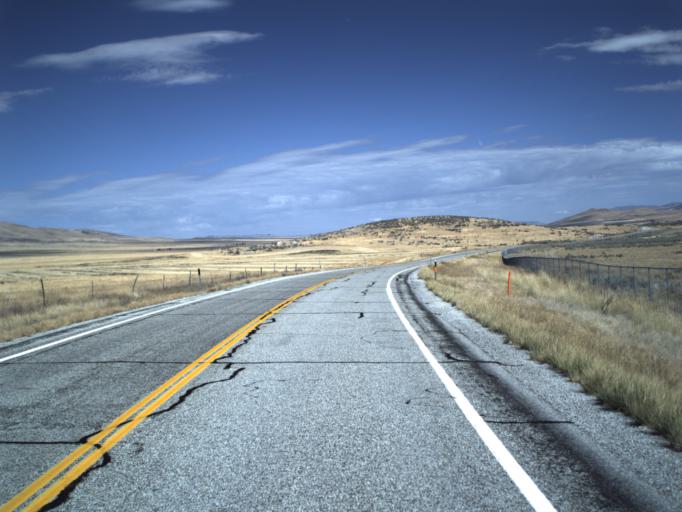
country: US
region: Utah
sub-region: Box Elder County
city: Tremonton
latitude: 41.7113
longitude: -112.4524
